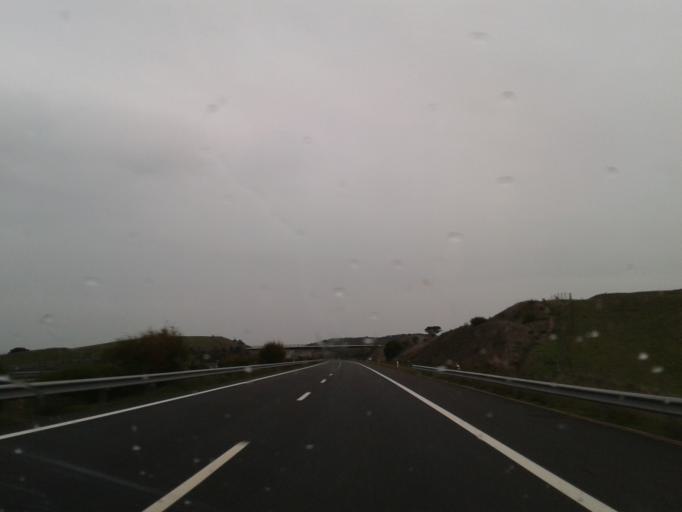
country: PT
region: Beja
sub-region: Aljustrel
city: Aljustrel
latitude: 37.8595
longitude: -8.2298
